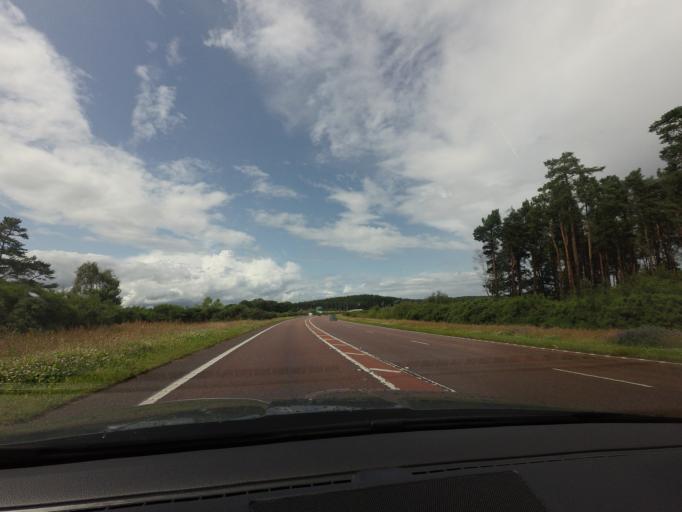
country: GB
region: Scotland
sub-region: Moray
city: Fochabers
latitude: 57.6240
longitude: -3.1375
